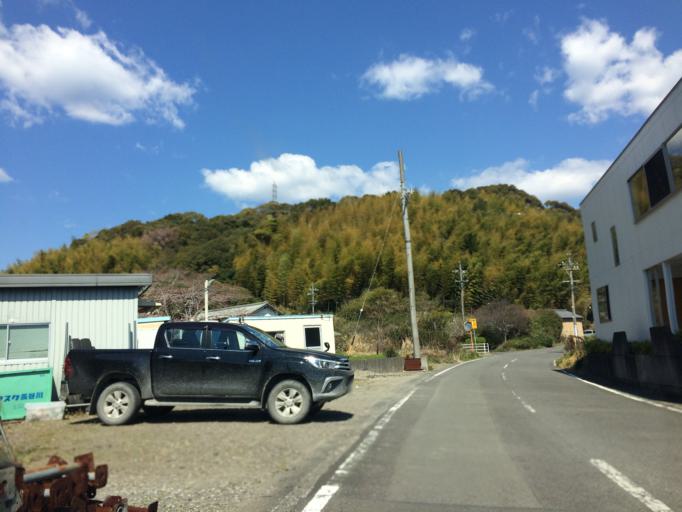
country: JP
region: Shizuoka
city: Fujieda
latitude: 34.8491
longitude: 138.2245
